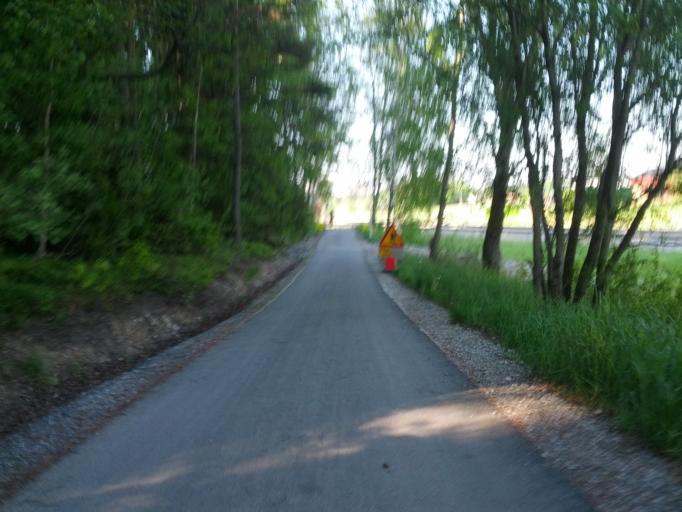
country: SE
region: Stockholm
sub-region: Taby Kommun
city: Taby
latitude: 59.4794
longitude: 18.0582
